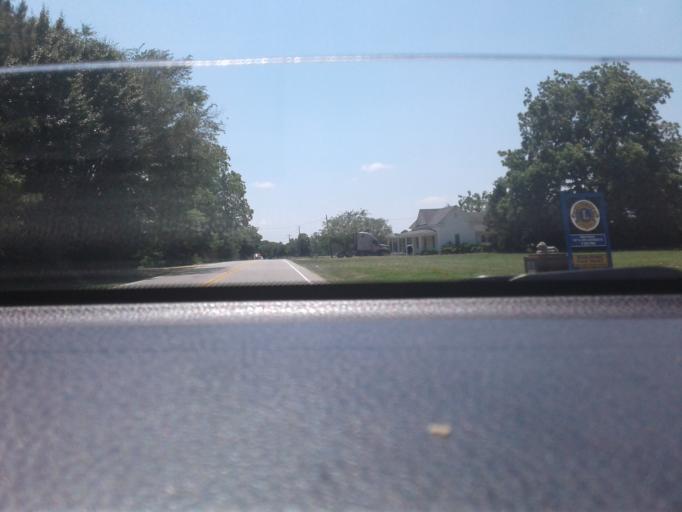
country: US
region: North Carolina
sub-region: Harnett County
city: Dunn
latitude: 35.3427
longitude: -78.5830
